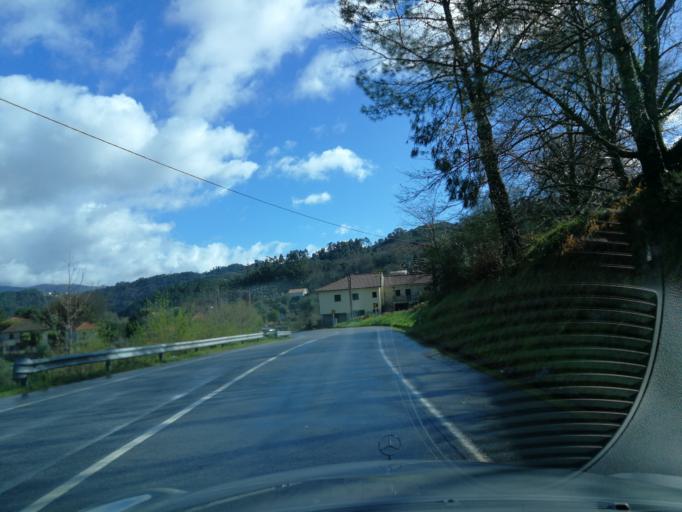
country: PT
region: Braga
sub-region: Terras de Bouro
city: Antas
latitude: 41.8357
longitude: -8.2963
